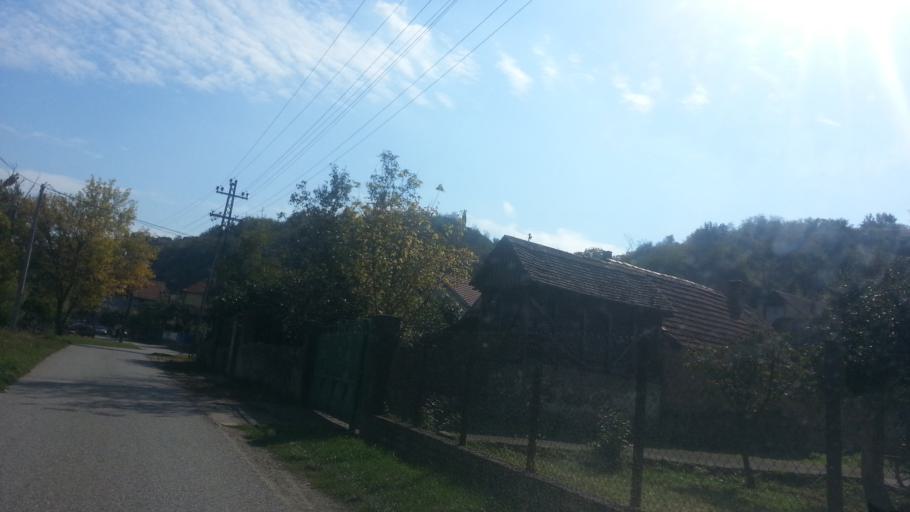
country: RS
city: Novi Slankamen
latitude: 45.1493
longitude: 20.2491
